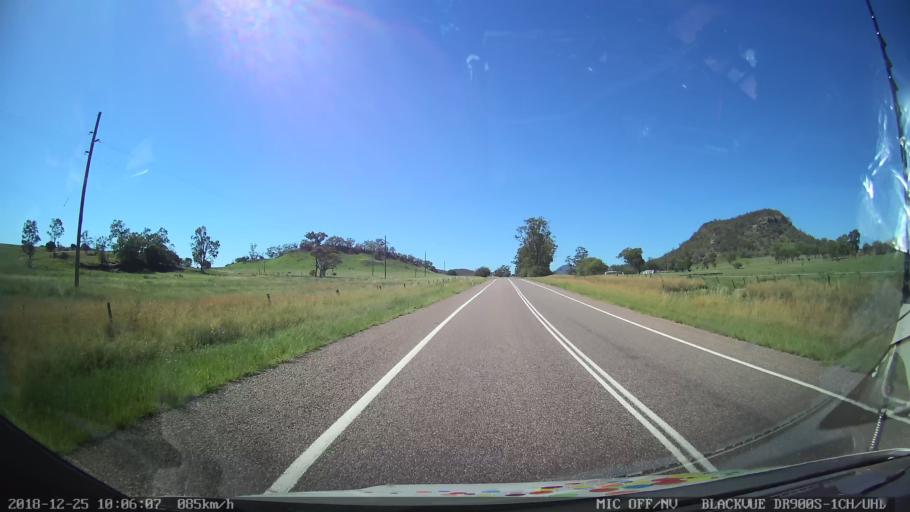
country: AU
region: New South Wales
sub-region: Upper Hunter Shire
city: Merriwa
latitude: -32.2561
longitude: 150.4888
